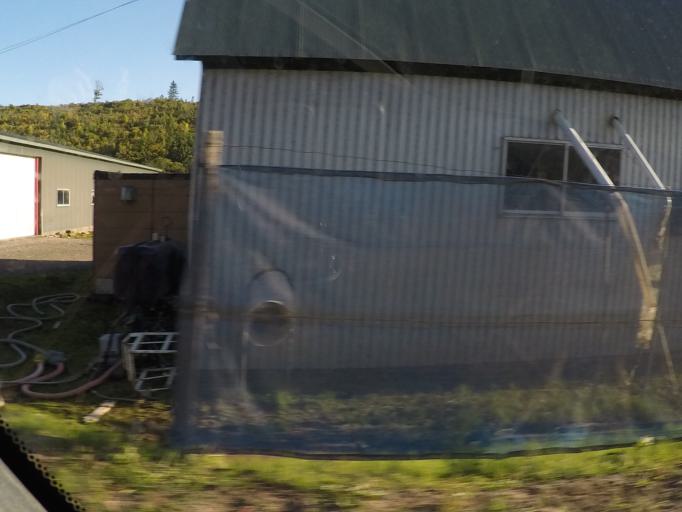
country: JP
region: Hokkaido
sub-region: Asahikawa-shi
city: Asahikawa
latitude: 43.6271
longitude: 142.5206
